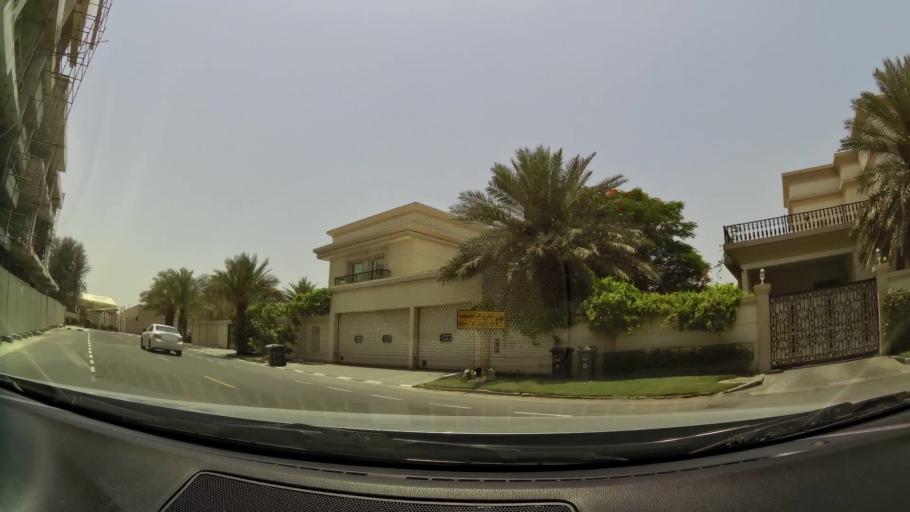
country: AE
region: Dubai
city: Dubai
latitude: 25.1663
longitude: 55.2350
